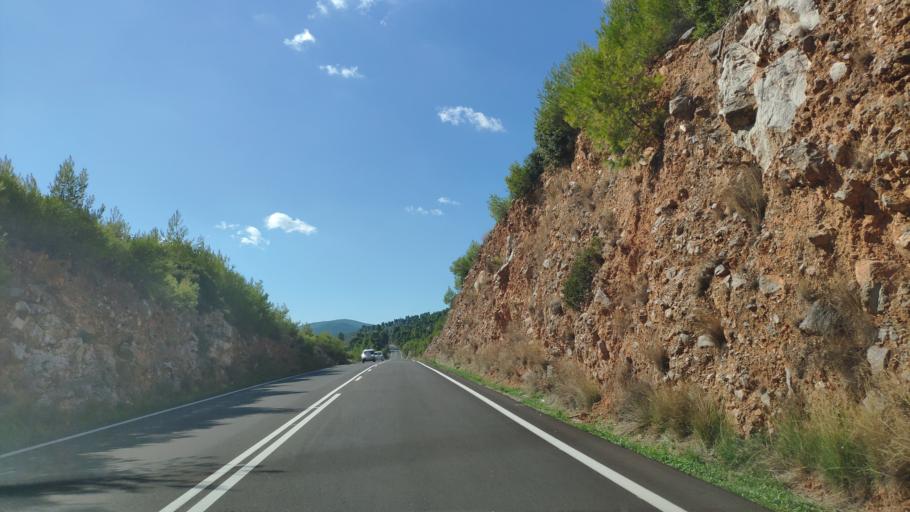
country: GR
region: Peloponnese
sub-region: Nomos Korinthias
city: Sofikon
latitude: 37.8179
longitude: 23.0963
